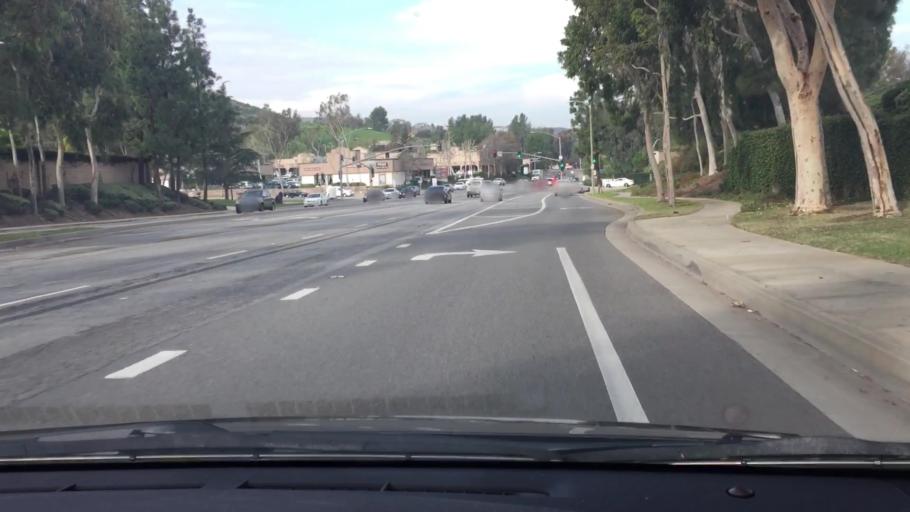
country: US
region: California
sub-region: Orange County
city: North Tustin
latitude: 33.7948
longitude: -117.7700
